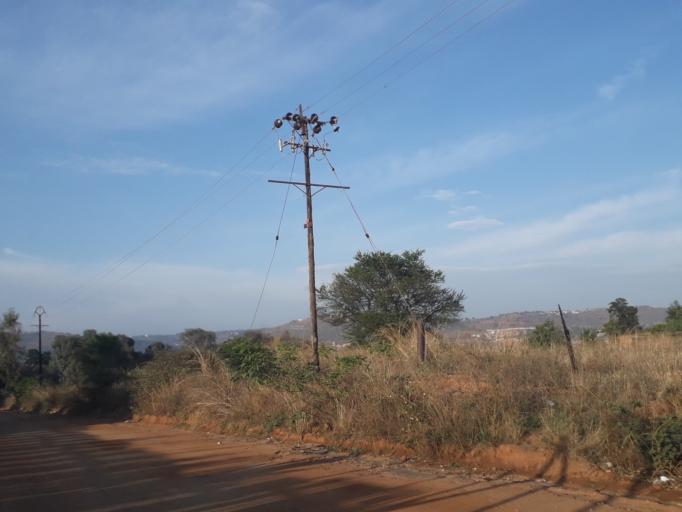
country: ZA
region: Gauteng
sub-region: City of Johannesburg Metropolitan Municipality
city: Roodepoort
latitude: -26.0927
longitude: 27.8982
